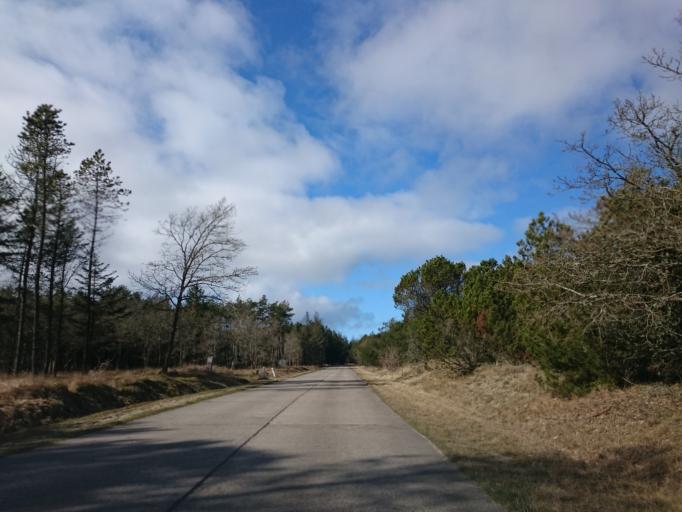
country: DK
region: North Denmark
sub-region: Frederikshavn Kommune
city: Skagen
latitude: 57.6540
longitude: 10.4263
